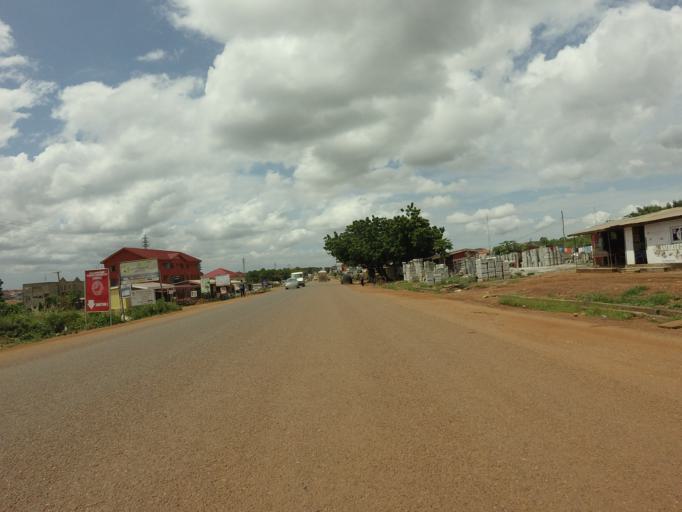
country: GH
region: Eastern
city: Aburi
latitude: 5.8120
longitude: -0.1228
